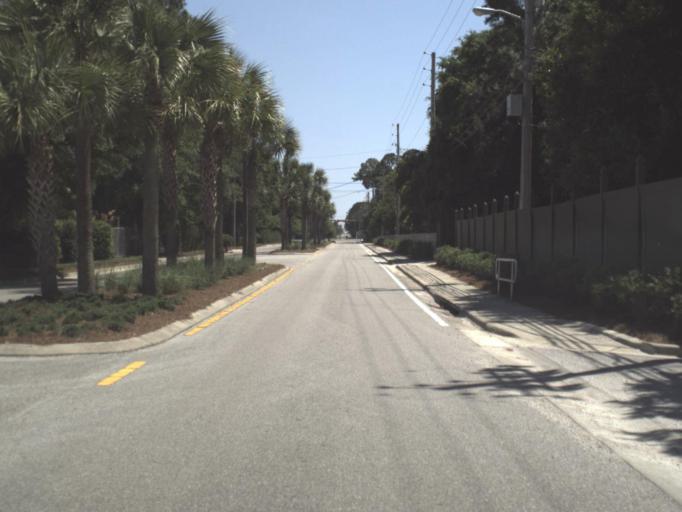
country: US
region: Florida
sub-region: Bay County
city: Pretty Bayou
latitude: 30.2013
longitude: -85.6833
